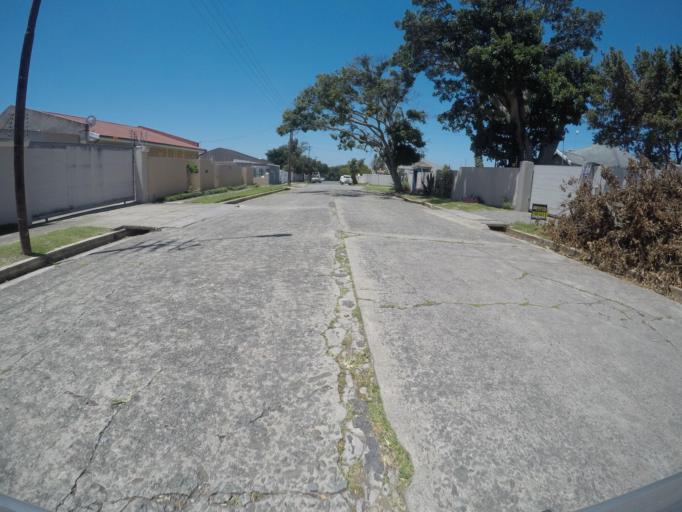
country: ZA
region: Eastern Cape
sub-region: Buffalo City Metropolitan Municipality
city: East London
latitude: -32.9887
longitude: 27.9087
